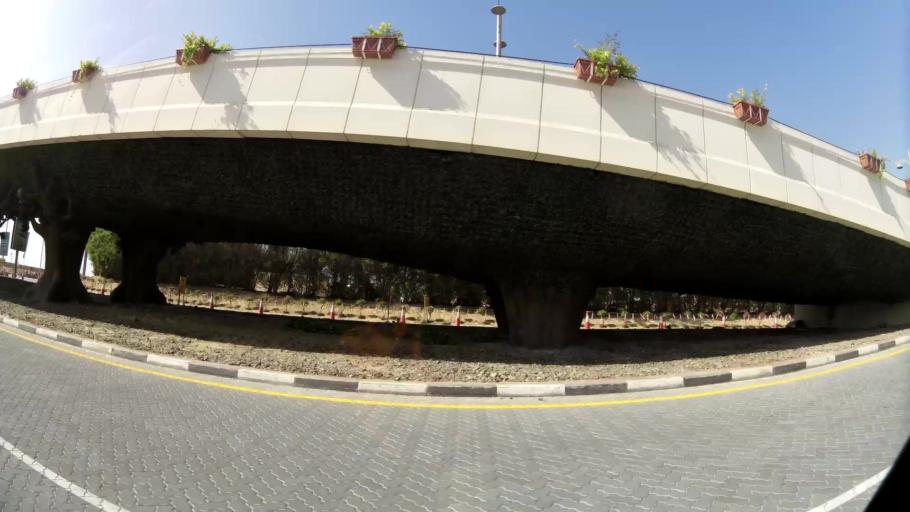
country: AE
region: Dubai
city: Dubai
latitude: 25.1255
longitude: 55.1127
